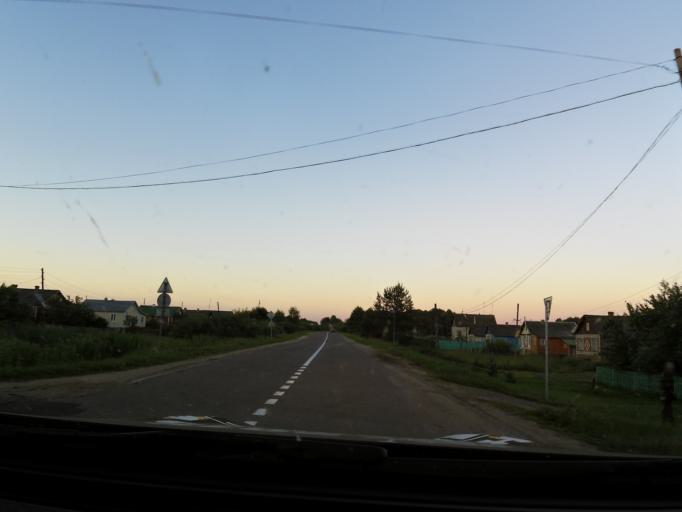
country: RU
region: Jaroslavl
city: Lyubim
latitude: 58.3231
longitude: 41.0173
